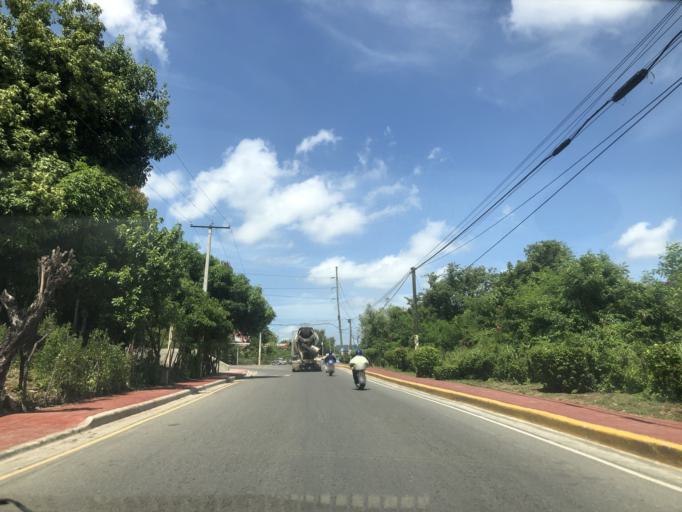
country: DO
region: Santiago
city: La Canela
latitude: 19.4522
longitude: -70.7684
